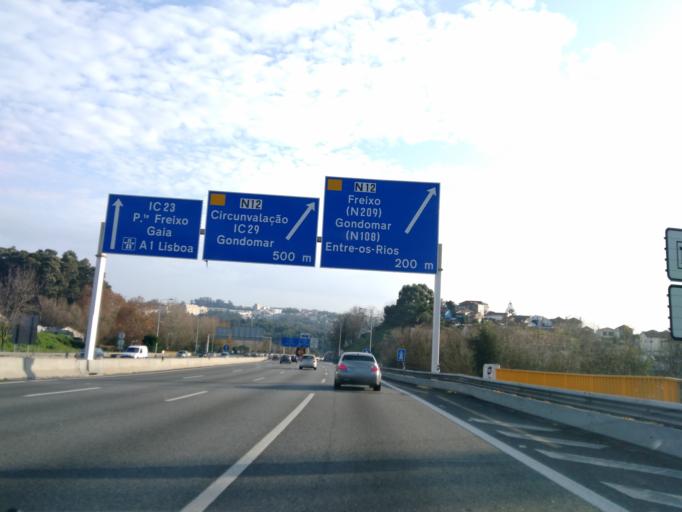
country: PT
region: Porto
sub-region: Gondomar
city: Valbom
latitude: 41.1535
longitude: -8.5821
